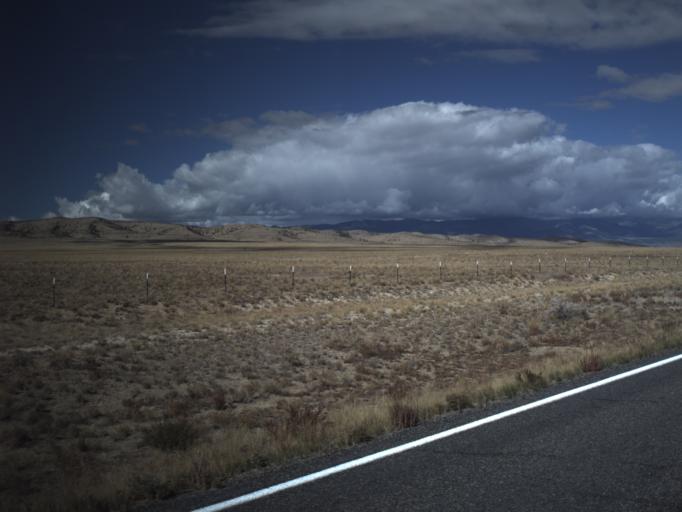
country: US
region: Utah
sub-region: Beaver County
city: Milford
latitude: 38.6724
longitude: -113.8860
